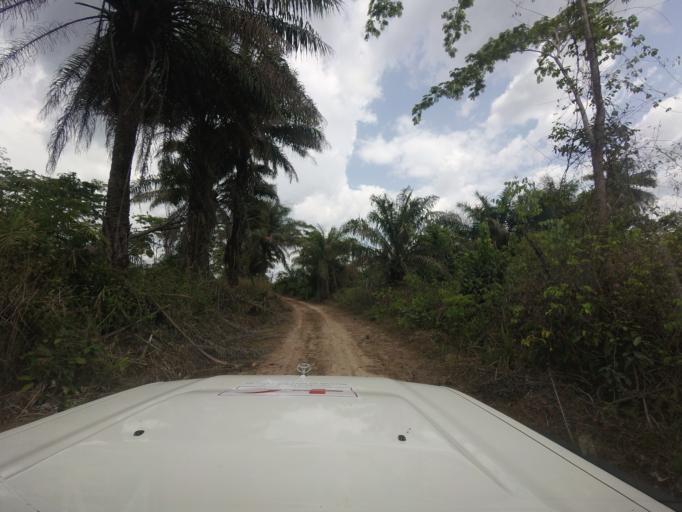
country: LR
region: Lofa
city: Voinjama
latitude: 8.3921
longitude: -9.6138
